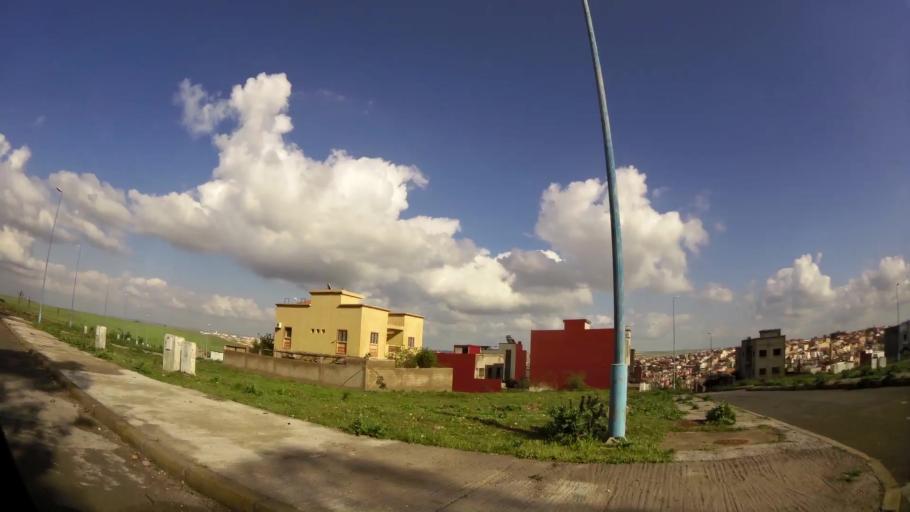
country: MA
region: Chaouia-Ouardigha
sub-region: Settat Province
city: Settat
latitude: 33.0149
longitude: -7.6323
